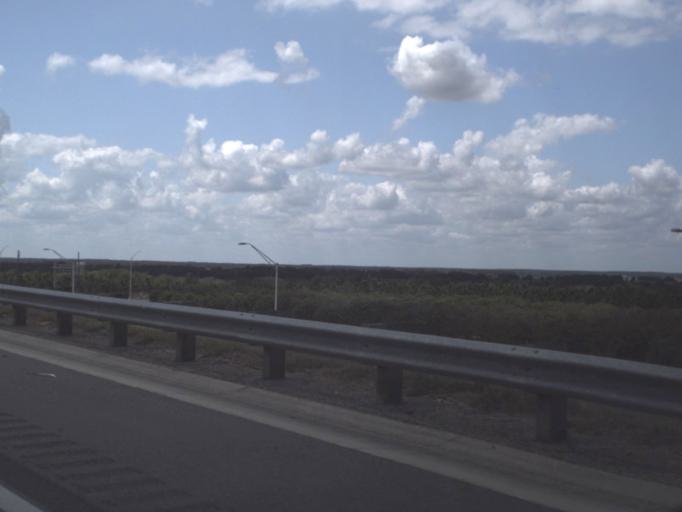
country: US
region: Florida
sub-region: Orange County
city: Oakland
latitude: 28.4508
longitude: -81.6424
